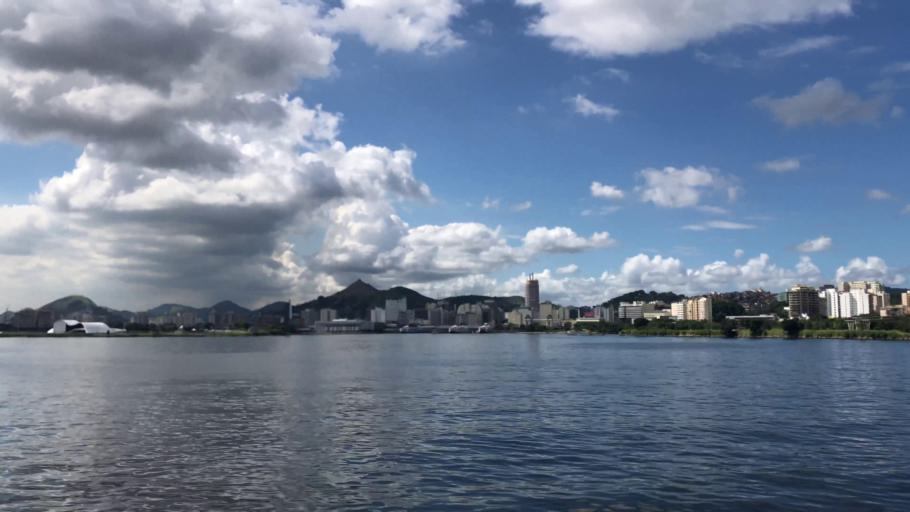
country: BR
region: Rio de Janeiro
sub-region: Niteroi
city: Niteroi
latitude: -22.8942
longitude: -43.1312
